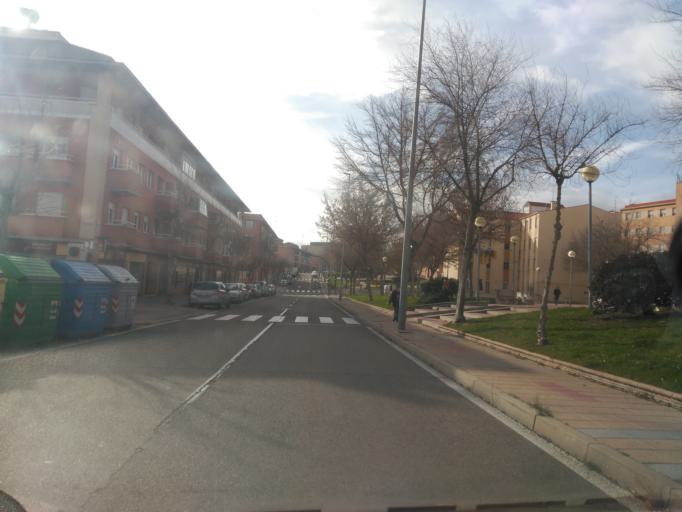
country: ES
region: Castille and Leon
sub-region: Provincia de Salamanca
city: Salamanca
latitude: 40.9633
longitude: -5.6487
